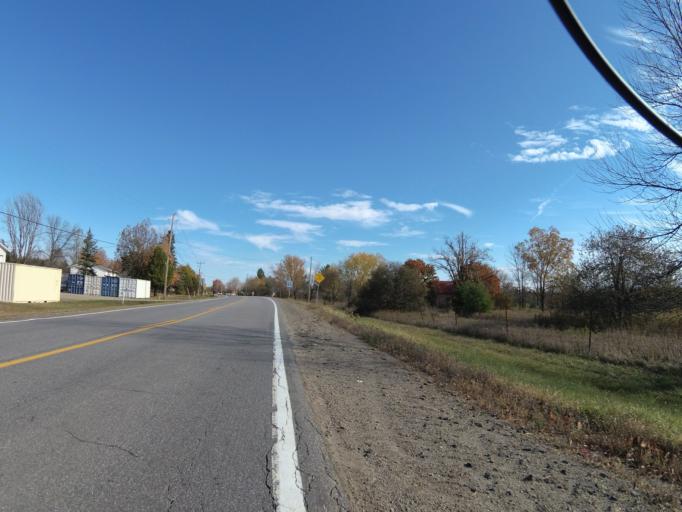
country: CA
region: Ontario
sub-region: Lanark County
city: Smiths Falls
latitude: 44.8392
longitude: -75.9428
